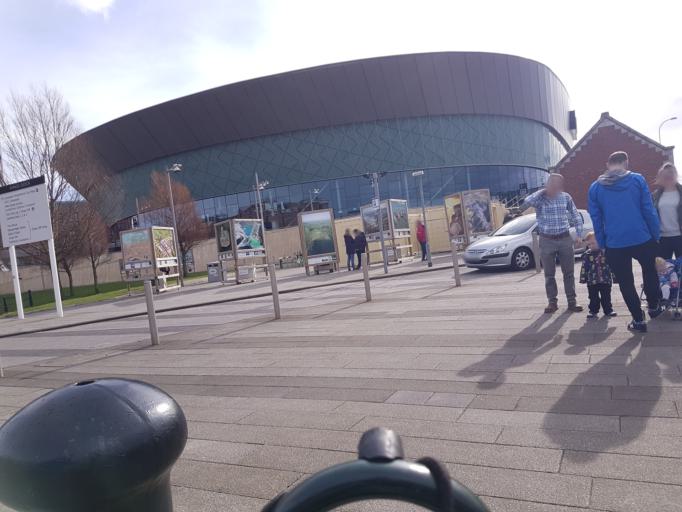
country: GB
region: England
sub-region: Liverpool
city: Liverpool
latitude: 53.3984
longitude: -2.9931
